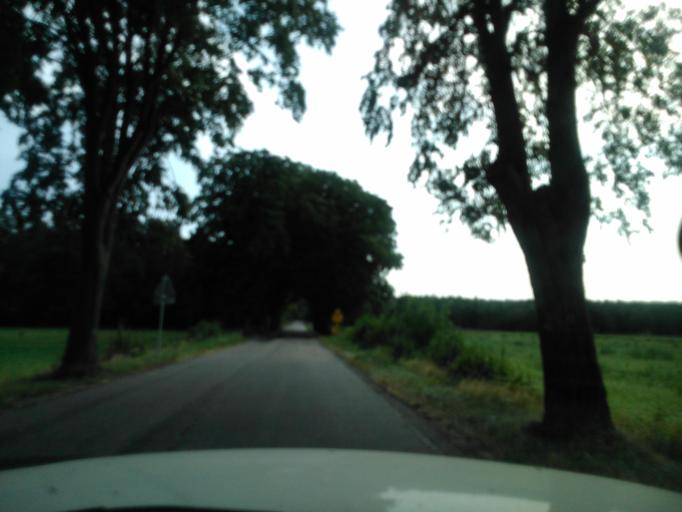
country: PL
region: Kujawsko-Pomorskie
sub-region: Powiat wabrzeski
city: Debowa Laka
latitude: 53.1967
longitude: 19.1608
